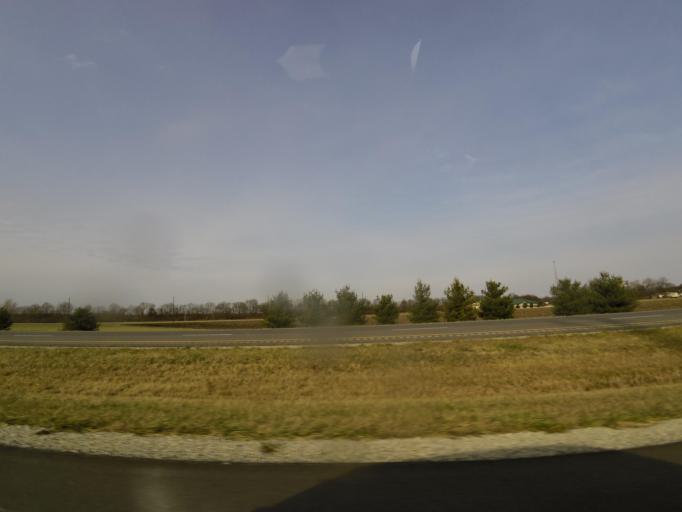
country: US
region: Illinois
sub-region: Shelby County
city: Moweaqua
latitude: 39.6128
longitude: -89.0210
